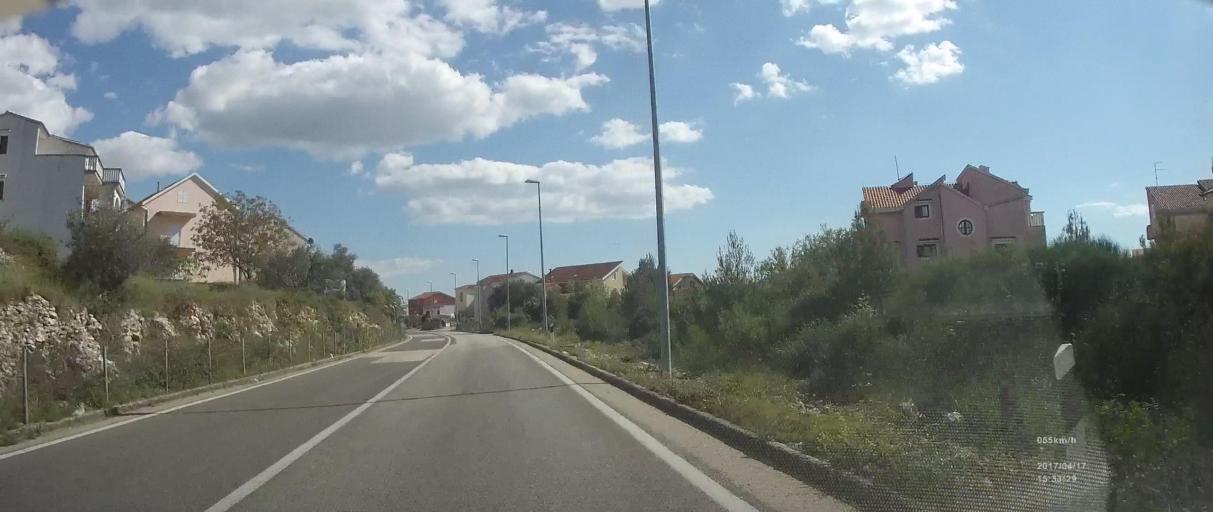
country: HR
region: Sibensko-Kniniska
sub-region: Grad Sibenik
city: Brodarica
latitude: 43.6858
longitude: 15.9116
